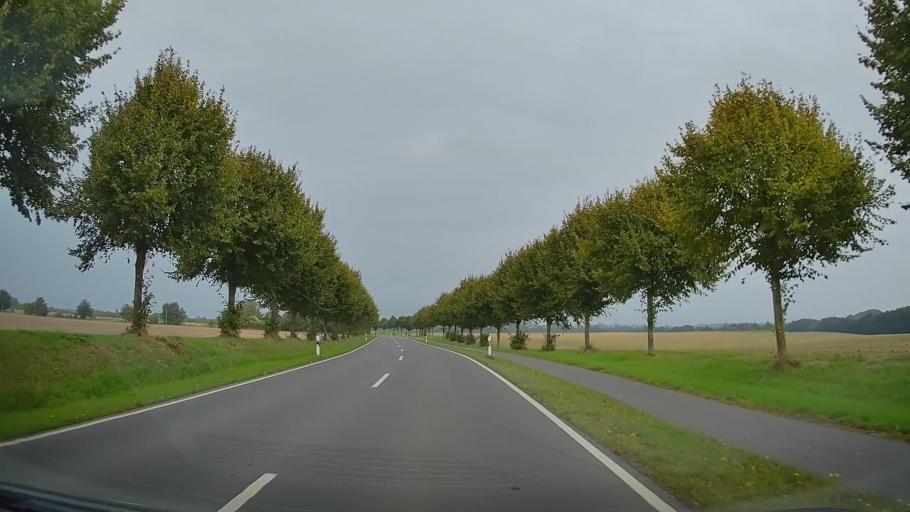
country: DE
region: Mecklenburg-Vorpommern
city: Ostseebad Kuhlungsborn
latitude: 54.1319
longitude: 11.7754
